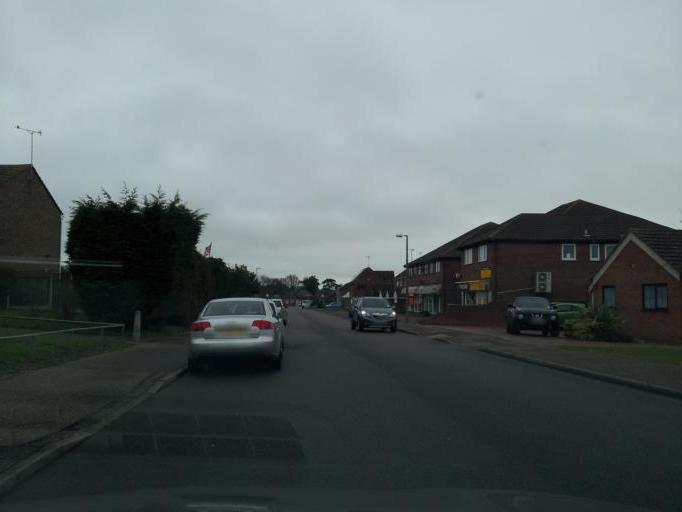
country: GB
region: England
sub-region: Essex
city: Dovercourt
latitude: 51.9273
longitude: 1.2538
